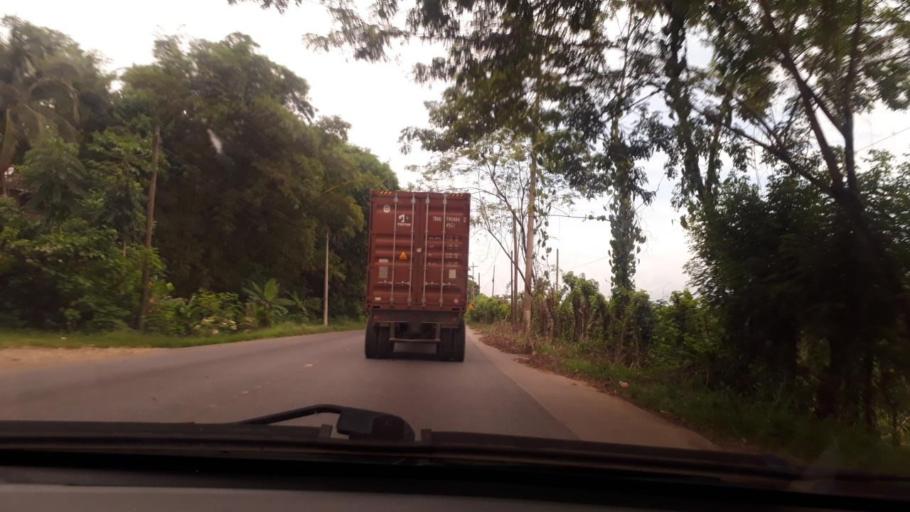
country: GT
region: Izabal
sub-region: Municipio de Puerto Barrios
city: Puerto Barrios
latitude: 15.5976
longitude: -88.5721
